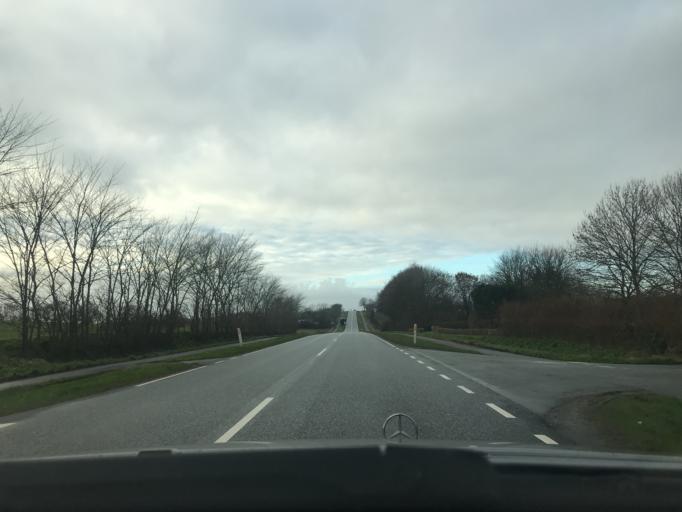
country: DK
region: South Denmark
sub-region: Sonderborg Kommune
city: Dybbol
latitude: 54.9085
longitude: 9.7347
